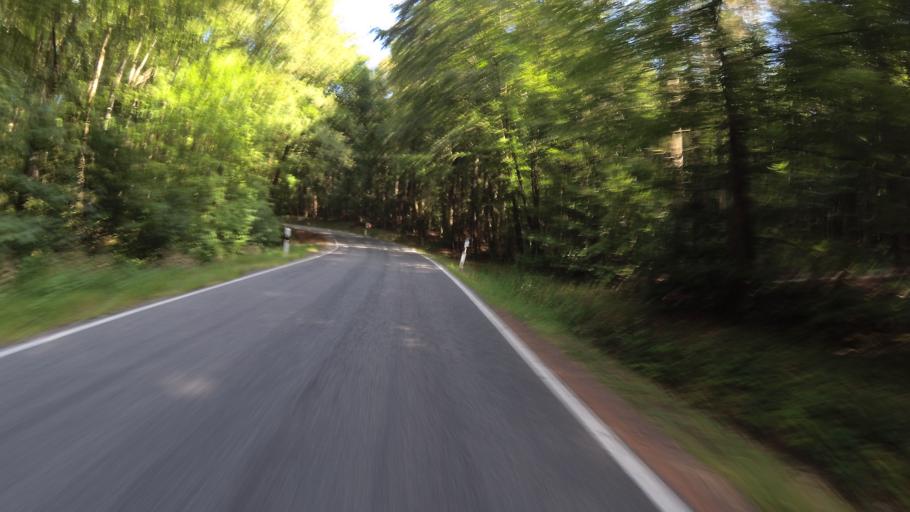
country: DE
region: Saarland
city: Gersheim
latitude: 49.1342
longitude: 7.2443
